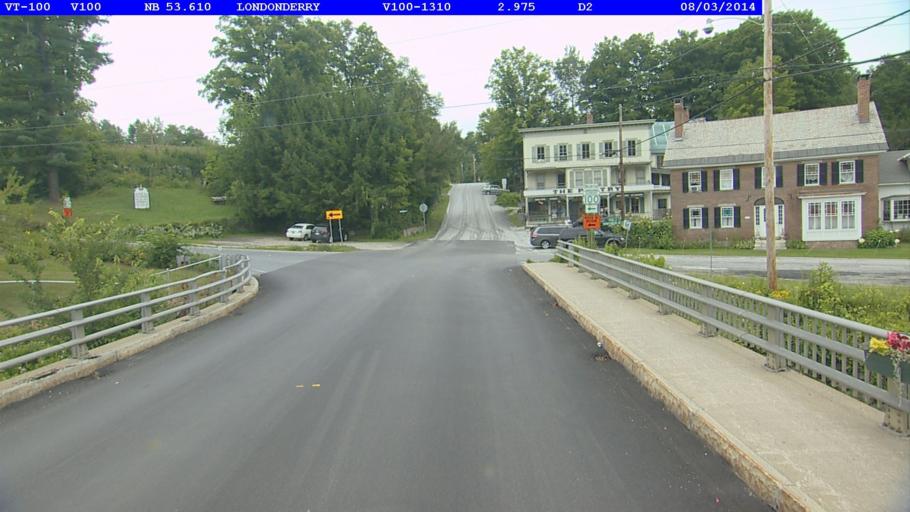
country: US
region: Vermont
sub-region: Windsor County
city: Chester
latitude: 43.1925
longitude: -72.8152
